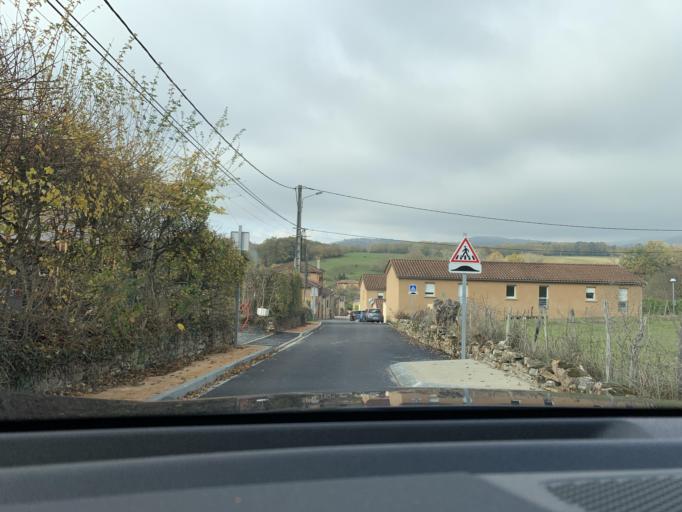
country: FR
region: Rhone-Alpes
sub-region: Departement du Rhone
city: Charnay
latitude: 45.9096
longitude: 4.6537
